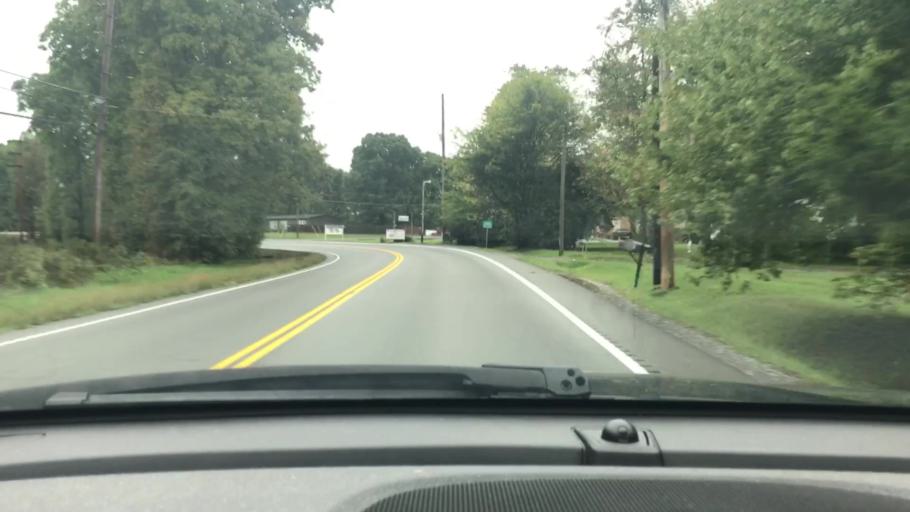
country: US
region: Tennessee
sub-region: Cheatham County
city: Kingston Springs
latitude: 36.1131
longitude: -87.1571
